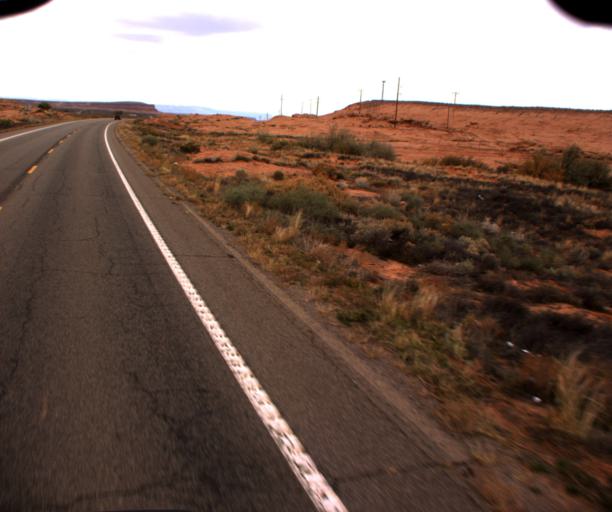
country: US
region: Arizona
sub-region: Navajo County
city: Kayenta
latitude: 36.8246
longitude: -109.8676
